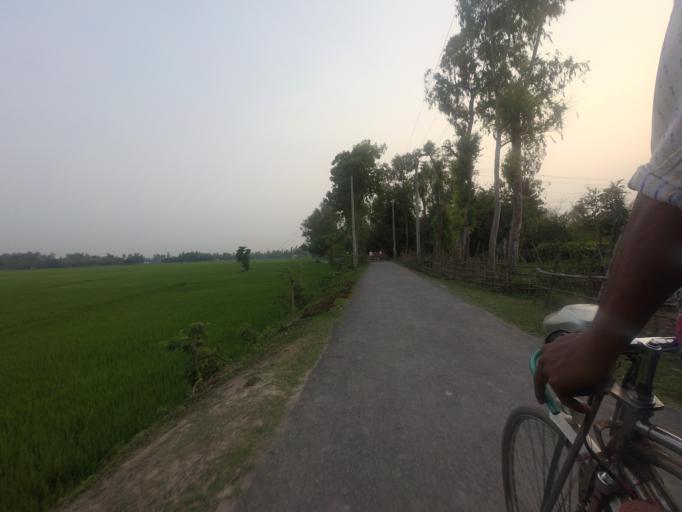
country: BD
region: Rajshahi
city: Sirajganj
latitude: 24.3271
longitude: 89.6772
